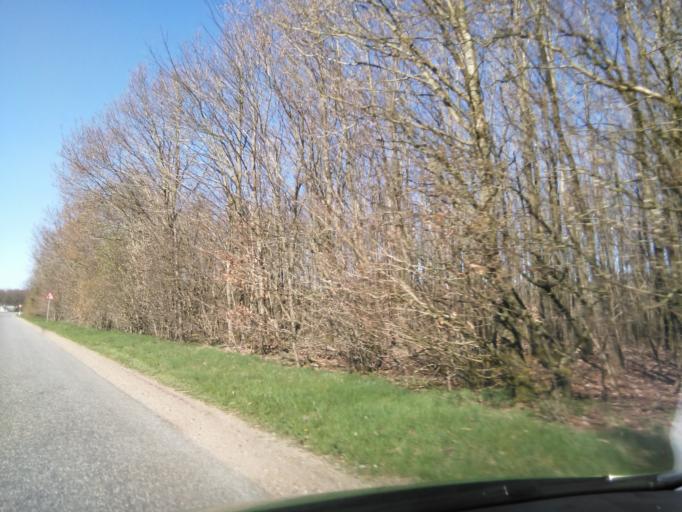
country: DK
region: South Denmark
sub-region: Billund Kommune
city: Billund
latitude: 55.7106
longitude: 9.1001
